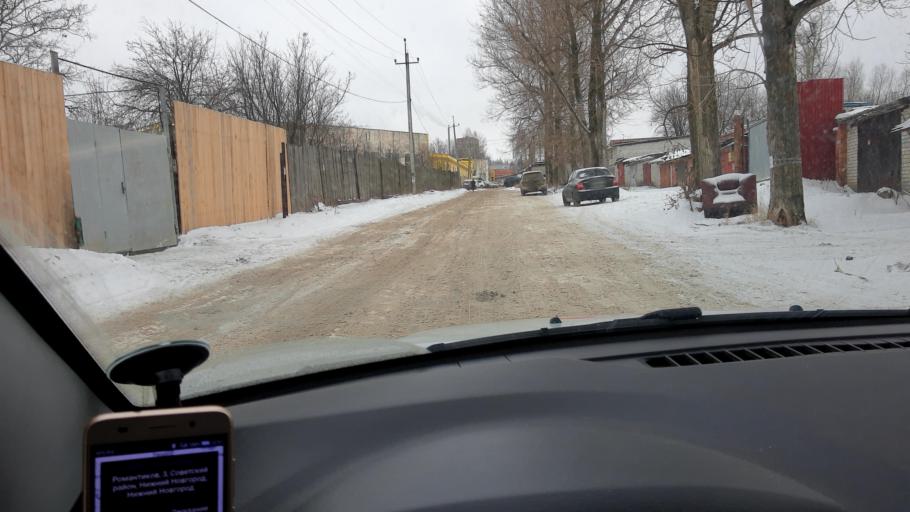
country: RU
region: Nizjnij Novgorod
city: Nizhniy Novgorod
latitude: 56.2484
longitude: 43.9603
